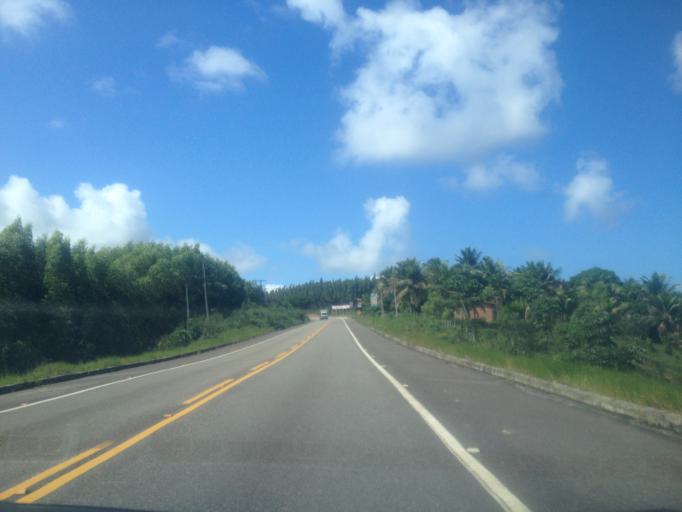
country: BR
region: Sergipe
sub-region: Indiaroba
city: Indiaroba
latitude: -11.4865
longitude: -37.4733
